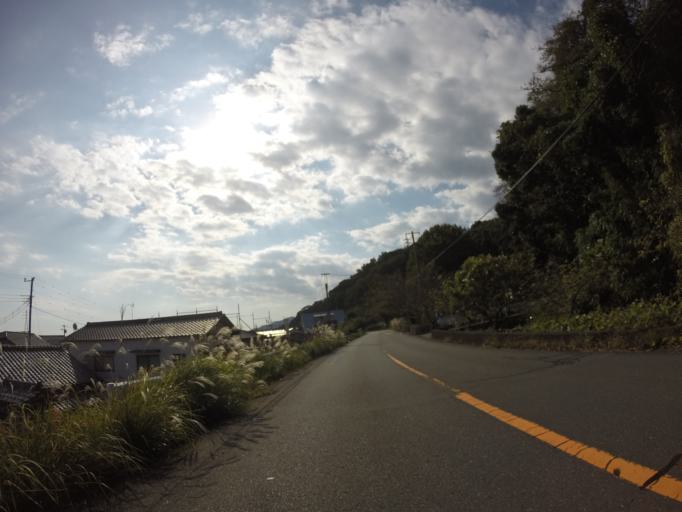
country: JP
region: Shizuoka
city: Fujinomiya
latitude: 35.1822
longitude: 138.6410
